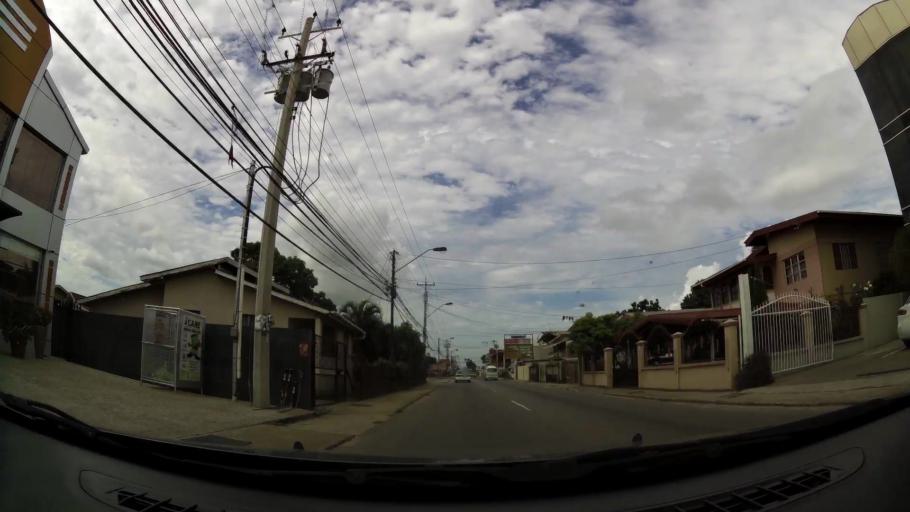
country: TT
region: Couva-Tabaquite-Talparo
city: Couva
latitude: 10.4221
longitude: -61.4634
